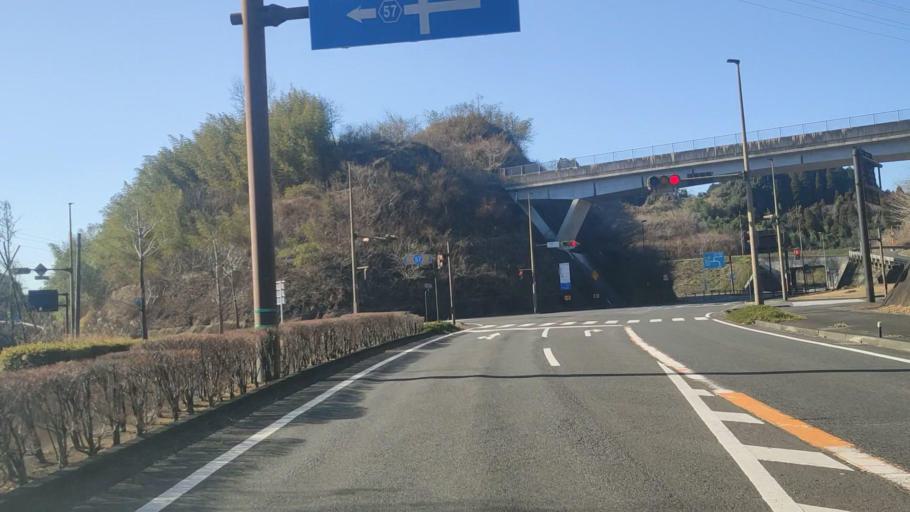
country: JP
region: Oita
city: Oita
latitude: 33.0709
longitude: 131.6319
